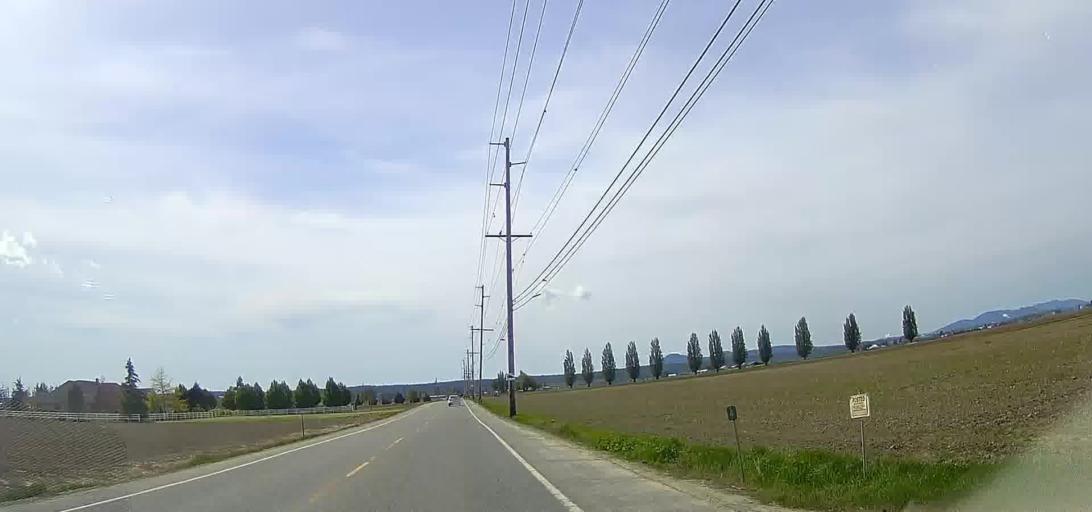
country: US
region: Washington
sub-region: Skagit County
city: Mount Vernon
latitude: 48.4209
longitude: -122.4358
